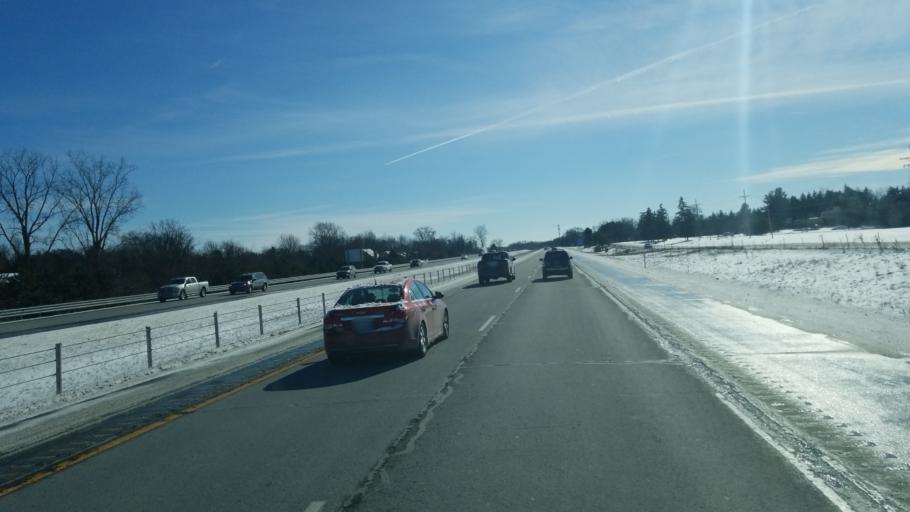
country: US
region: Michigan
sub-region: Livingston County
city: Brighton
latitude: 42.4917
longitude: -83.7576
